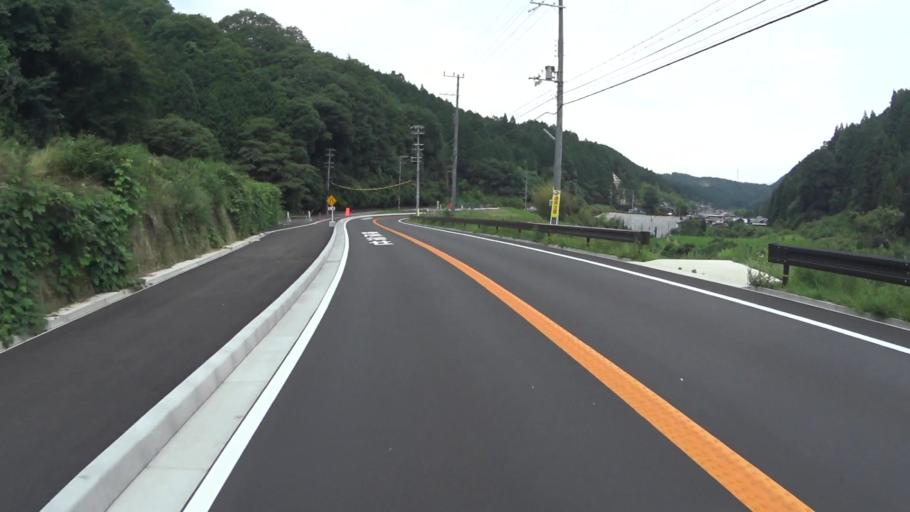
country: JP
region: Kyoto
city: Uji
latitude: 34.8525
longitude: 135.9273
